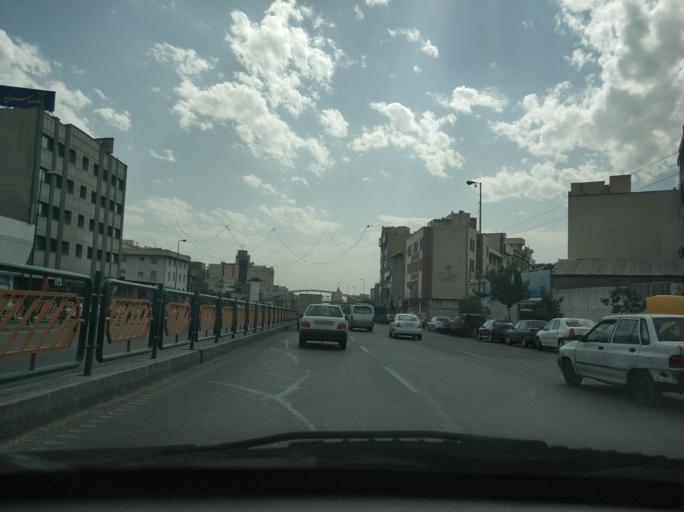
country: IR
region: Tehran
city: Tehran
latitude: 35.7202
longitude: 51.5082
